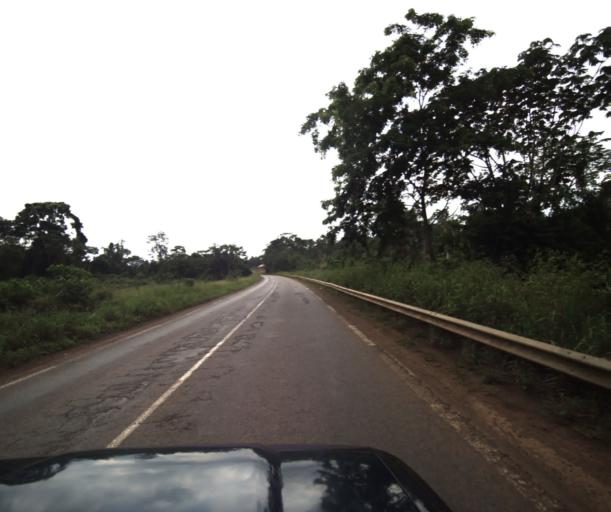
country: CM
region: Centre
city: Eseka
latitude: 3.8929
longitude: 10.7216
